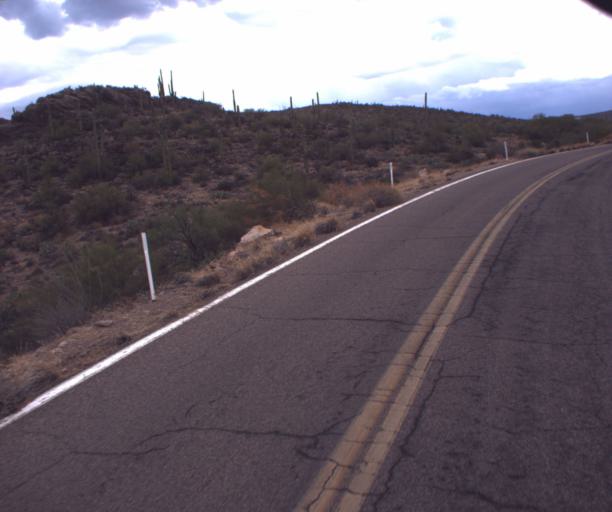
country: US
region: Arizona
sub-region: Pinal County
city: Apache Junction
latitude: 33.5438
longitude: -111.3399
